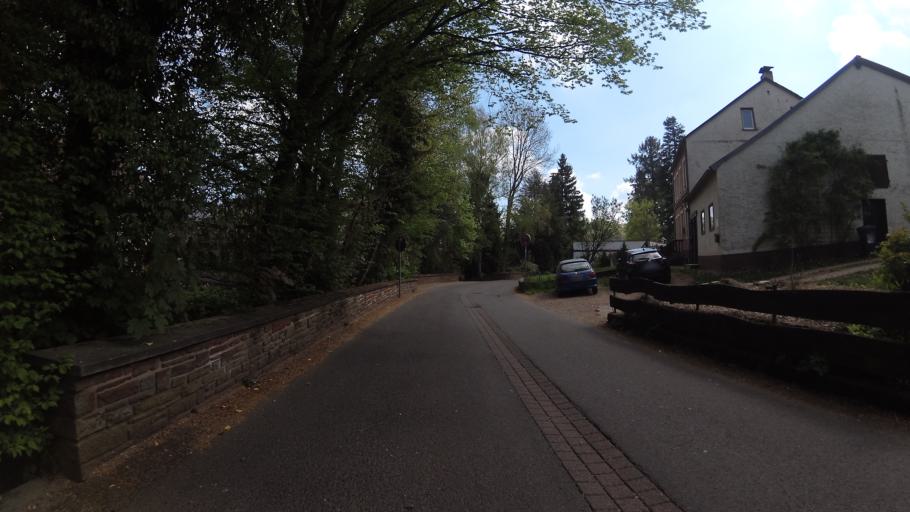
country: DE
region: Saarland
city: Wadern
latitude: 49.5371
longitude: 6.8898
